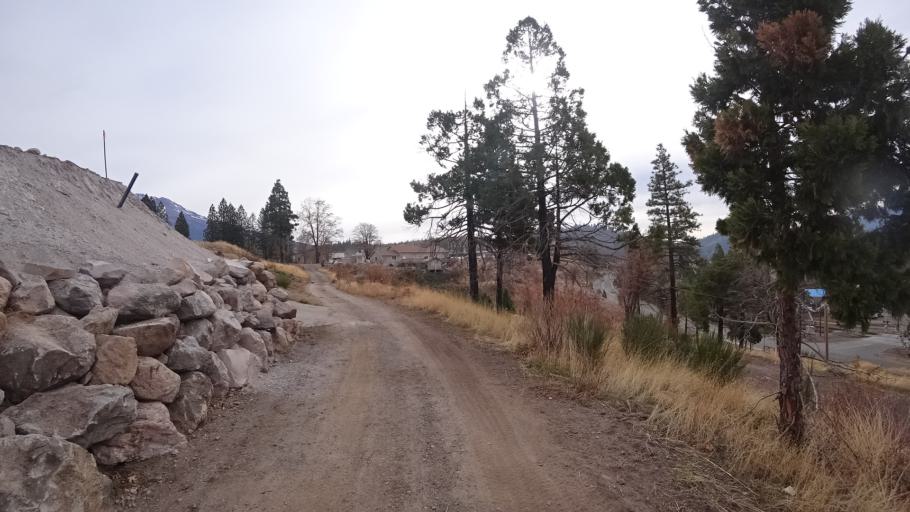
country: US
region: California
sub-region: Siskiyou County
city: Weed
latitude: 41.4294
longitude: -122.3827
